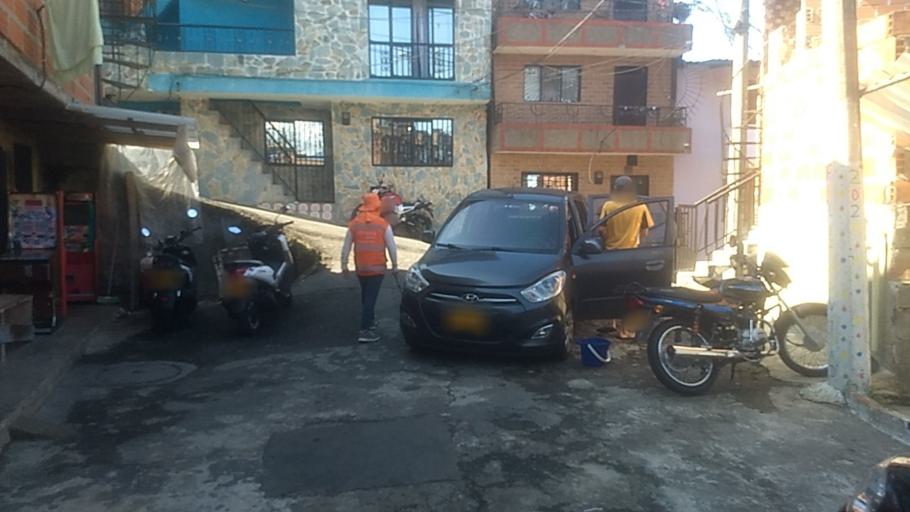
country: CO
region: Antioquia
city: Bello
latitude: 6.2959
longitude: -75.5496
